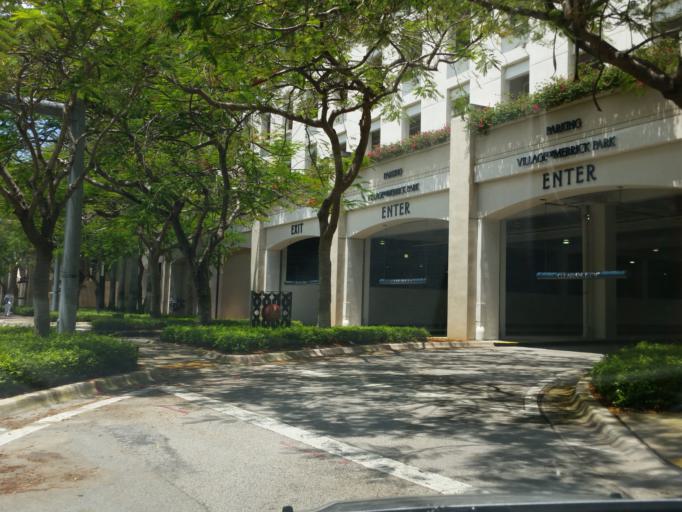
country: US
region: Florida
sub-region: Miami-Dade County
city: Coral Gables
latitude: 25.7305
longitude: -80.2618
